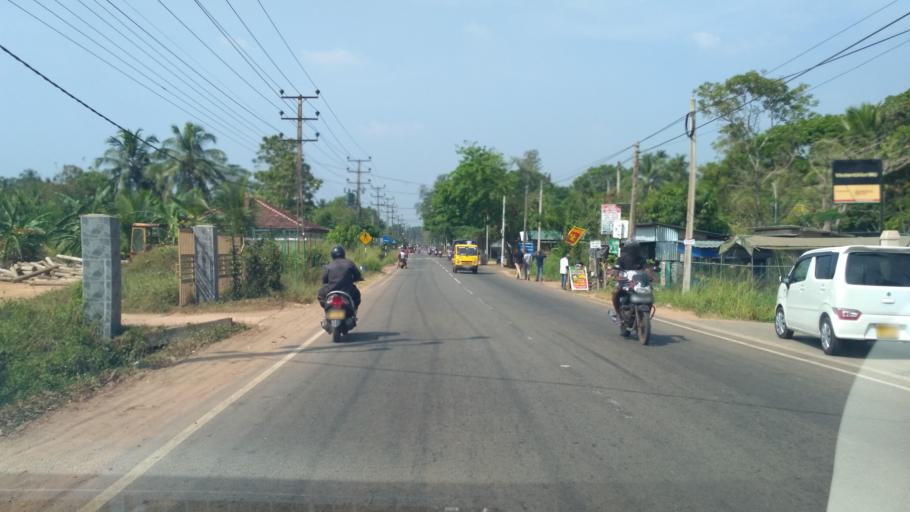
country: LK
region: Western
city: Minuwangoda
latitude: 7.3214
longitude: 79.9753
